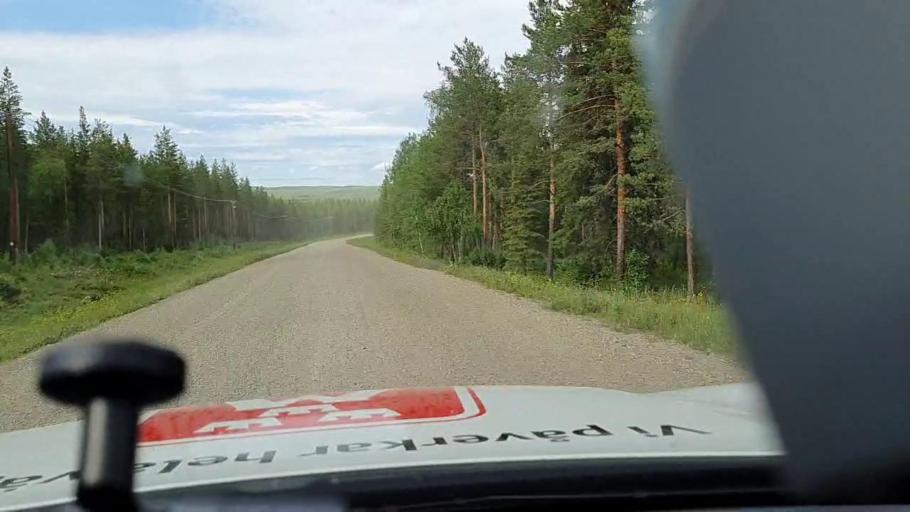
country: SE
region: Norrbotten
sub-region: Alvsbyns Kommun
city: AElvsbyn
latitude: 66.1432
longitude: 21.0184
